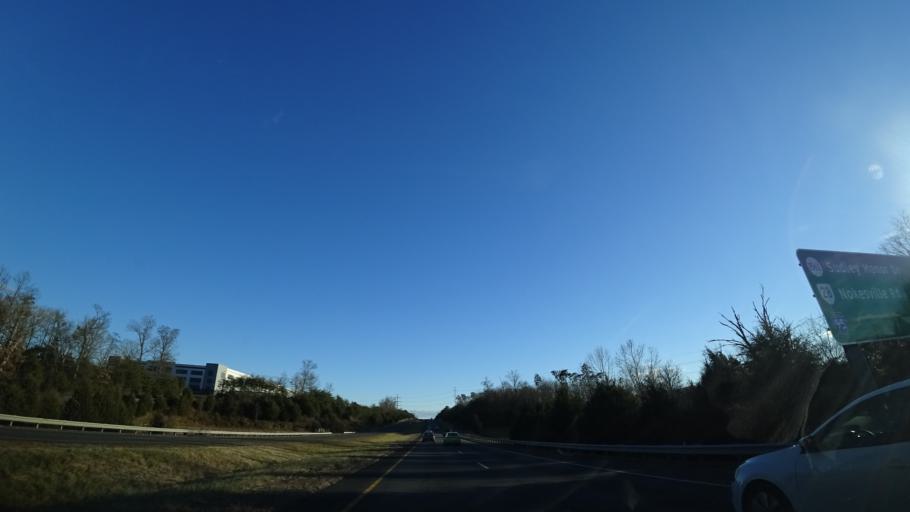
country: US
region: Virginia
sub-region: Prince William County
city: Bull Run
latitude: 38.7816
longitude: -77.5462
